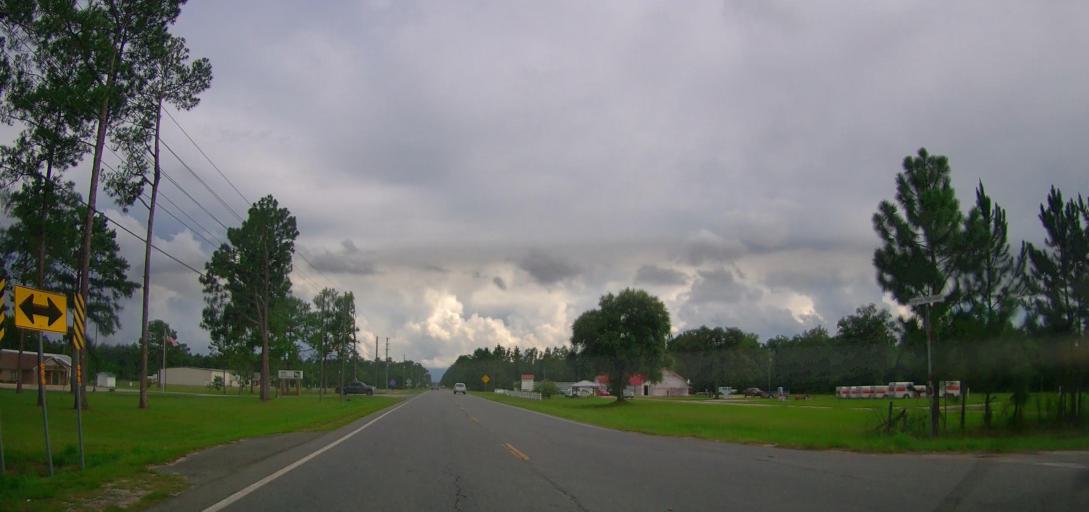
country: US
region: Georgia
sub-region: Wayne County
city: Jesup
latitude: 31.6446
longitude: -81.9072
